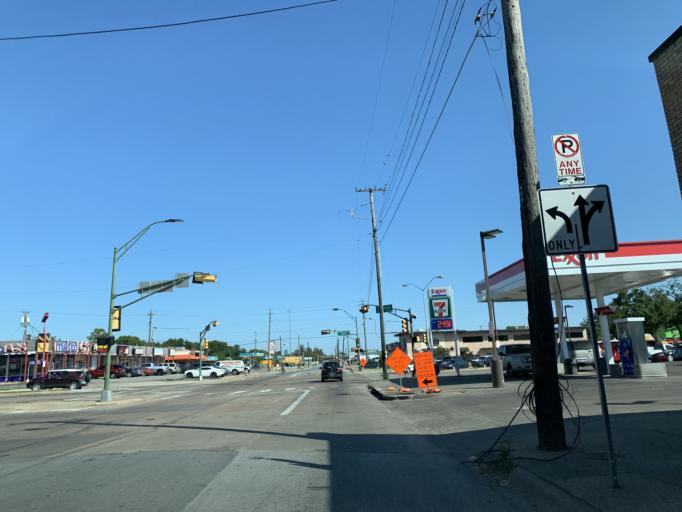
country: US
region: Texas
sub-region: Dallas County
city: Dallas
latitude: 32.7920
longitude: -96.7680
